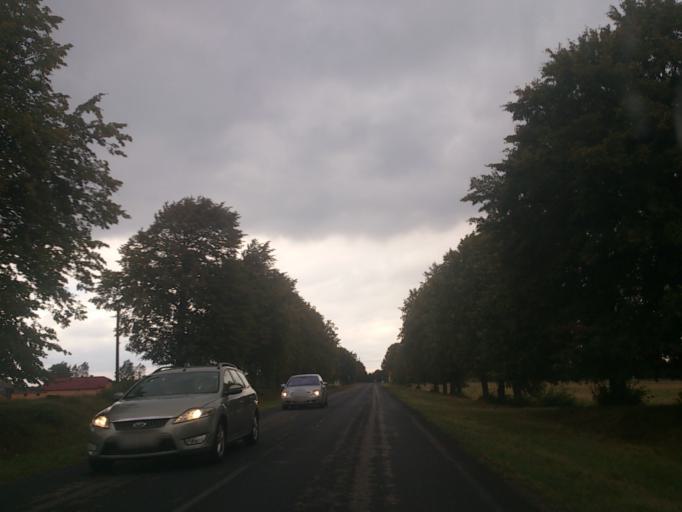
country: PL
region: Kujawsko-Pomorskie
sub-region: Powiat golubsko-dobrzynski
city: Golub-Dobrzyn
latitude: 53.0710
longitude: 19.0678
